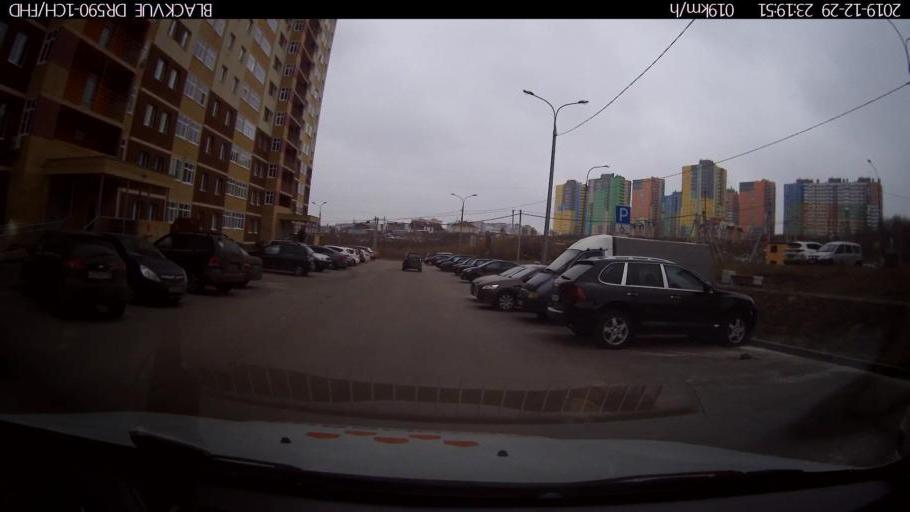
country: RU
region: Nizjnij Novgorod
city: Afonino
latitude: 56.2808
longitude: 44.0891
